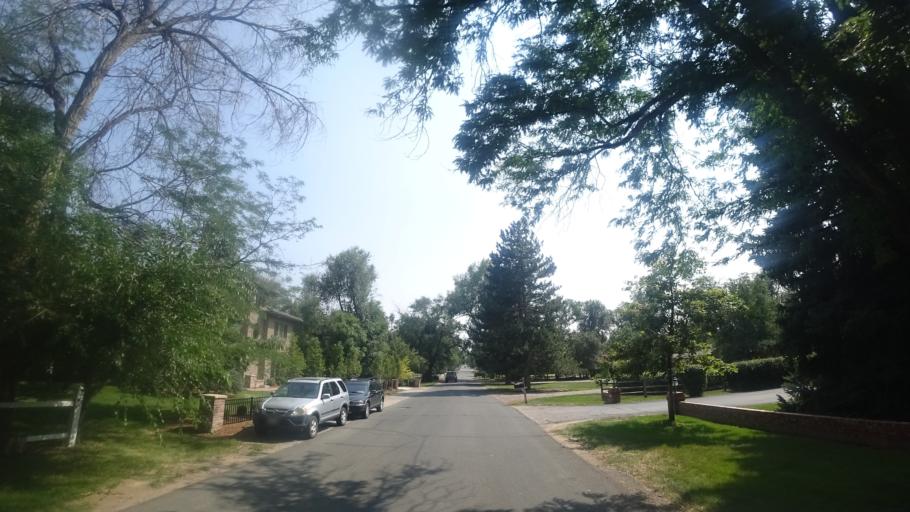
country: US
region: Colorado
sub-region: Arapahoe County
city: Cherry Hills Village
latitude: 39.6273
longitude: -104.9691
